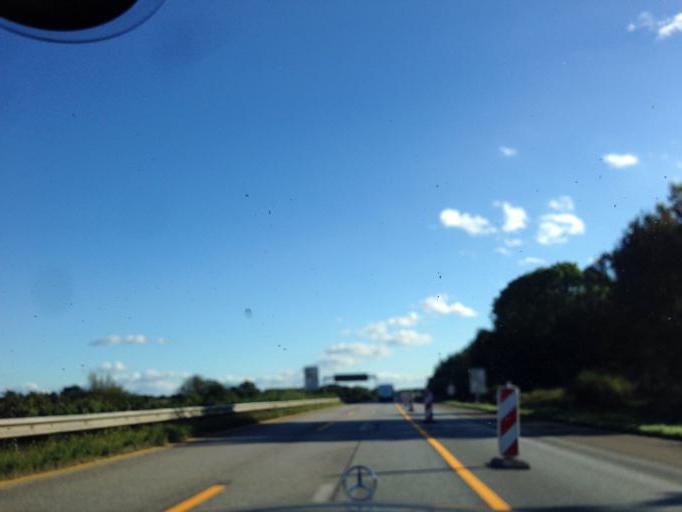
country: DE
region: Schleswig-Holstein
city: Schonbek
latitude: 54.1601
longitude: 9.9636
